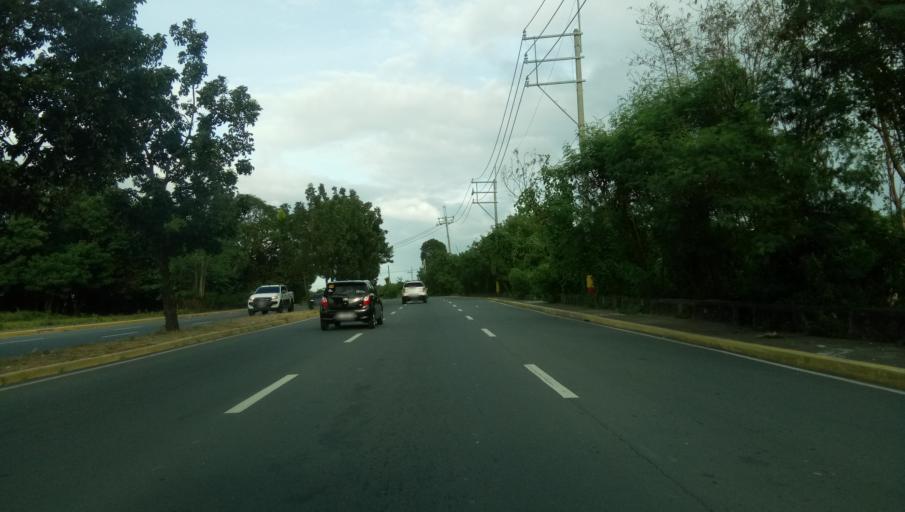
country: PH
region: Calabarzon
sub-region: Province of Cavite
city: Dasmarinas
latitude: 14.3775
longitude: 120.9520
